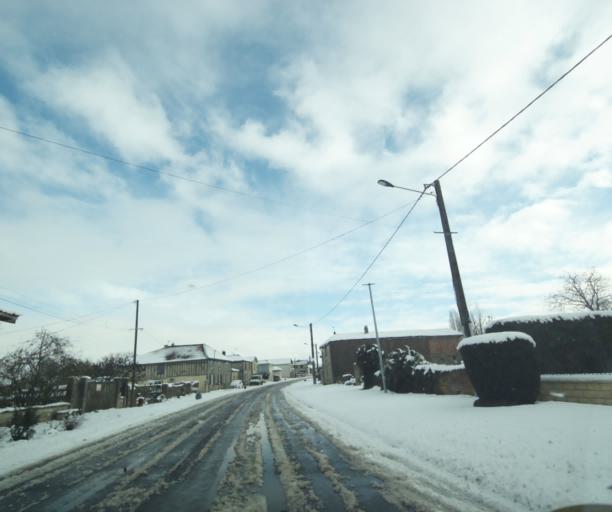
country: FR
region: Champagne-Ardenne
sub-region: Departement de la Haute-Marne
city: Montier-en-Der
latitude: 48.4548
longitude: 4.6788
